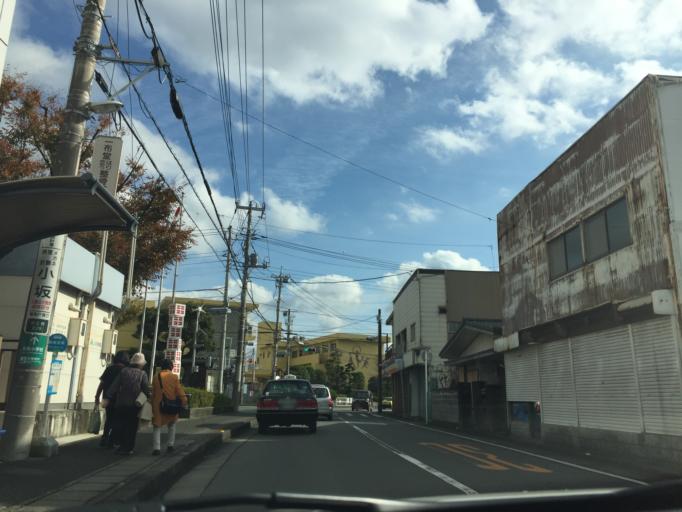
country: JP
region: Shizuoka
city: Mishima
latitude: 35.1374
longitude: 138.8971
